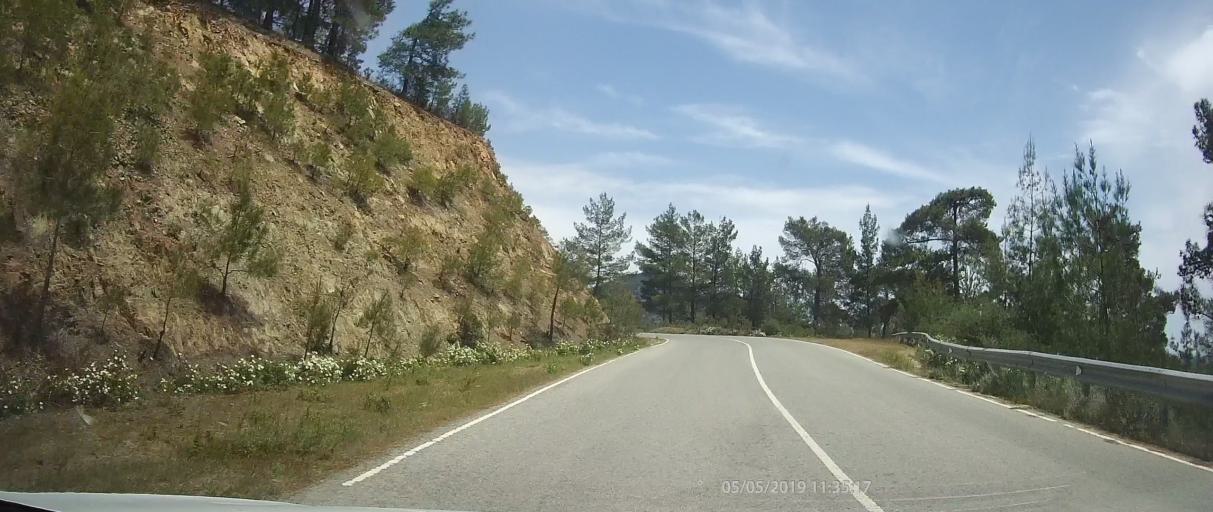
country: CY
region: Lefkosia
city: Kato Pyrgos
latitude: 34.9664
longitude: 32.6521
